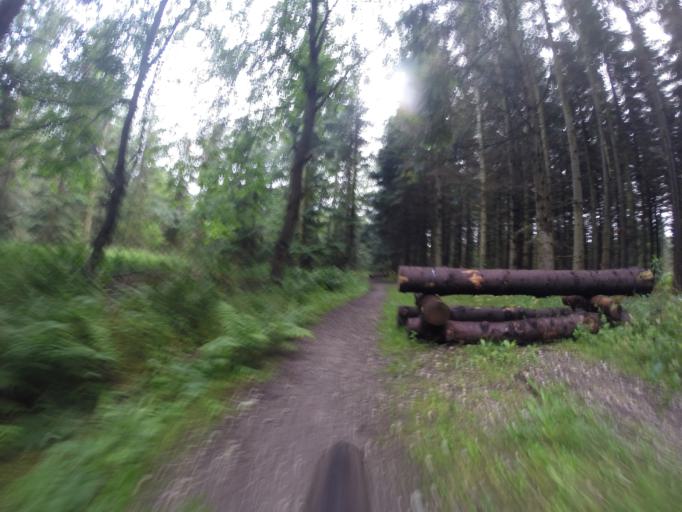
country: DK
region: Capital Region
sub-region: Ballerup Kommune
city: Ballerup
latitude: 55.7073
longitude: 12.3437
